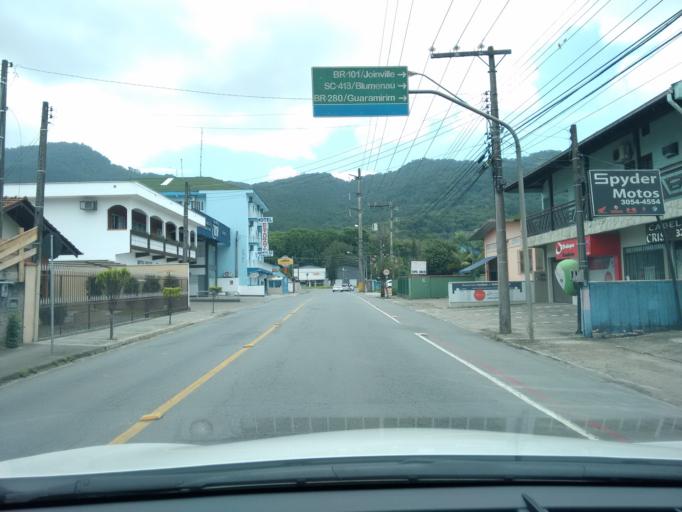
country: BR
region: Santa Catarina
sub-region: Jaragua Do Sul
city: Jaragua do Sul
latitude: -26.4814
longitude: -49.0566
